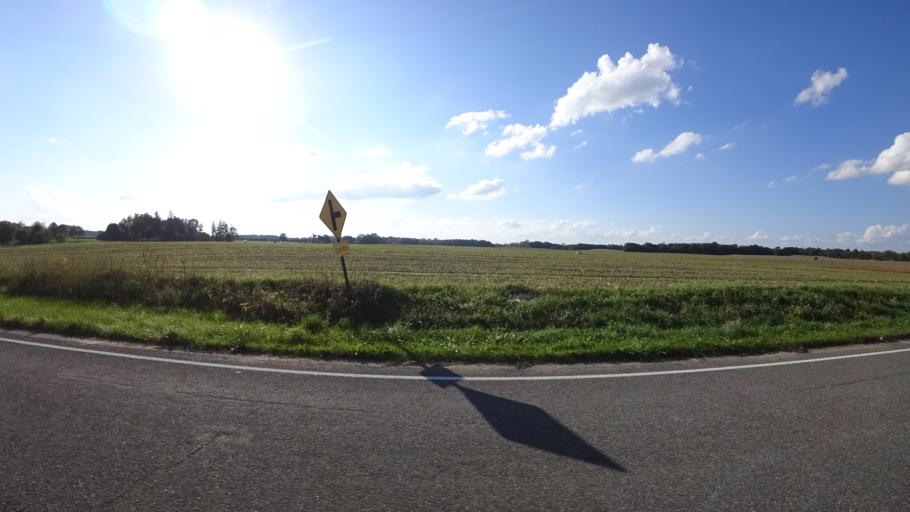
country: US
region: Michigan
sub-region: Saint Joseph County
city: Centreville
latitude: 41.8921
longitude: -85.5069
